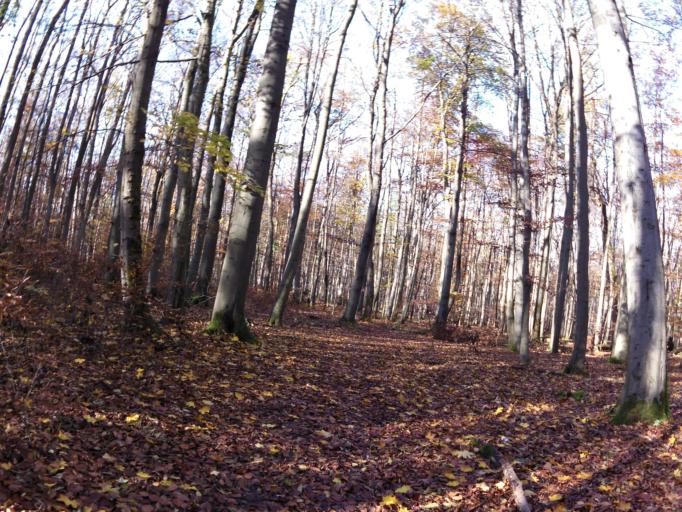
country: DE
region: Thuringia
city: Kammerforst
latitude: 51.0730
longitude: 10.4449
